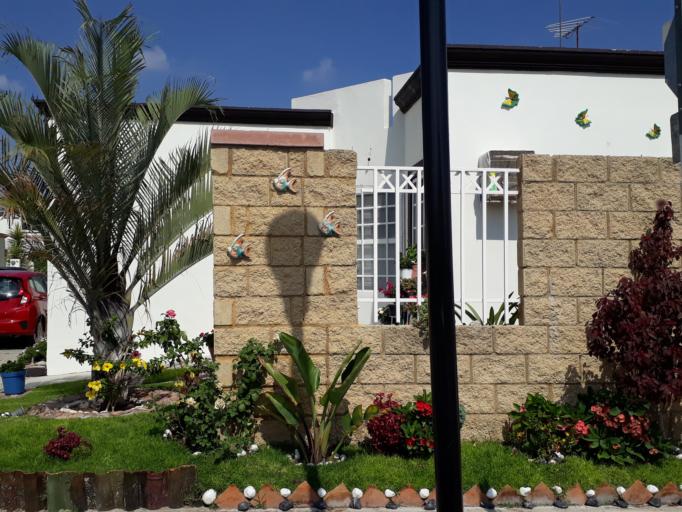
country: MX
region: Aguascalientes
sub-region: Aguascalientes
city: San Sebastian [Fraccionamiento]
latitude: 21.8084
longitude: -102.2930
